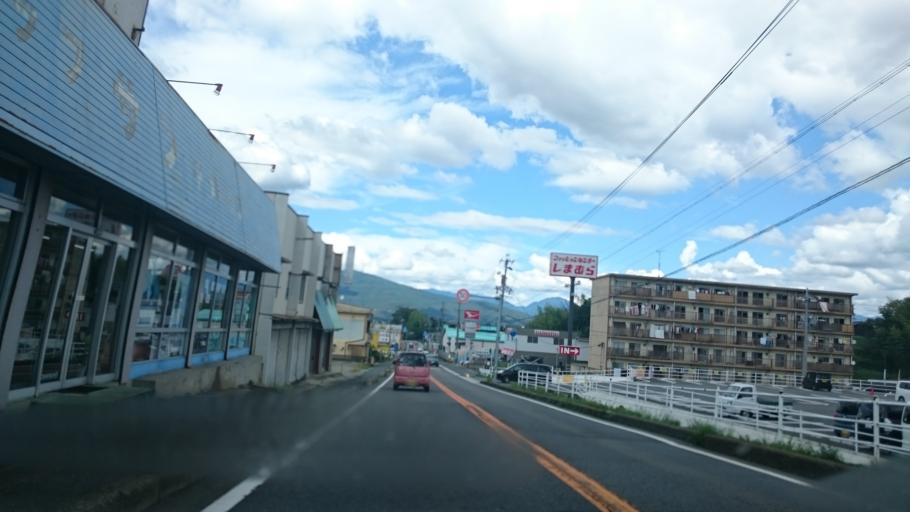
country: JP
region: Gifu
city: Nakatsugawa
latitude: 35.4820
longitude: 137.4858
